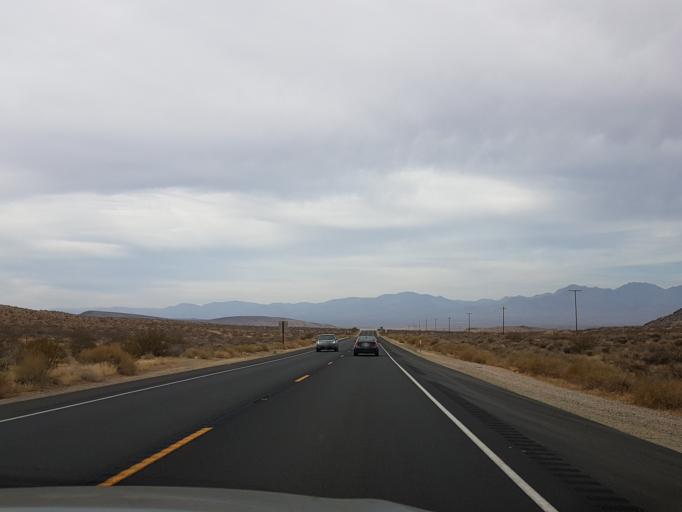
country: US
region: California
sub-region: Kern County
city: Ridgecrest
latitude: 35.5463
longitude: -117.6988
